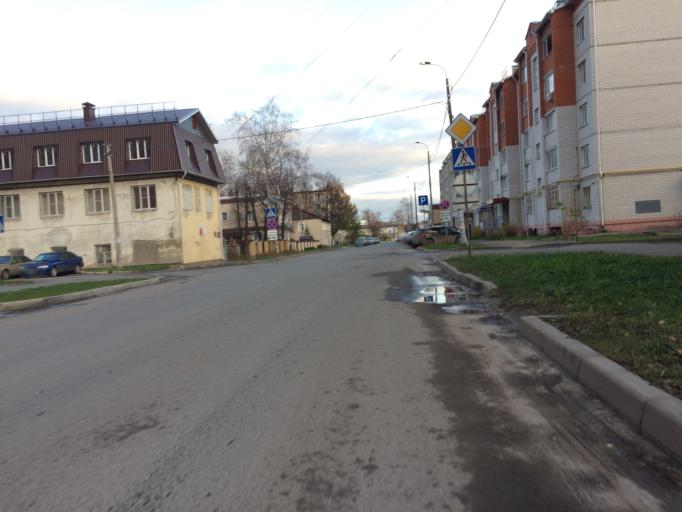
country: RU
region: Mariy-El
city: Yoshkar-Ola
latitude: 56.6472
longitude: 47.8973
